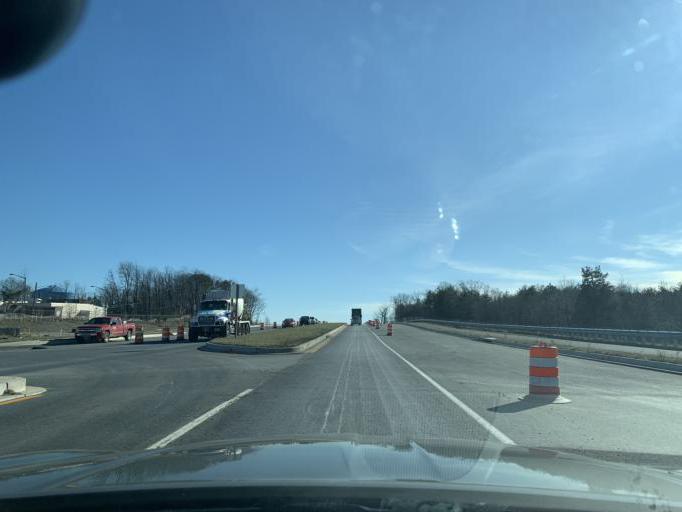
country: US
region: Maryland
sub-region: Anne Arundel County
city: Fort Meade
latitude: 39.1175
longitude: -76.7299
